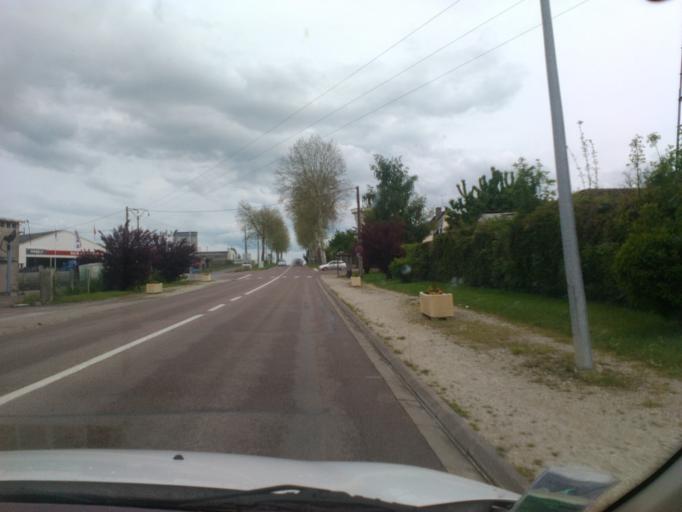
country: FR
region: Champagne-Ardenne
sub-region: Departement de l'Aube
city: Vendeuvre-sur-Barse
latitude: 48.2396
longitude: 4.4752
